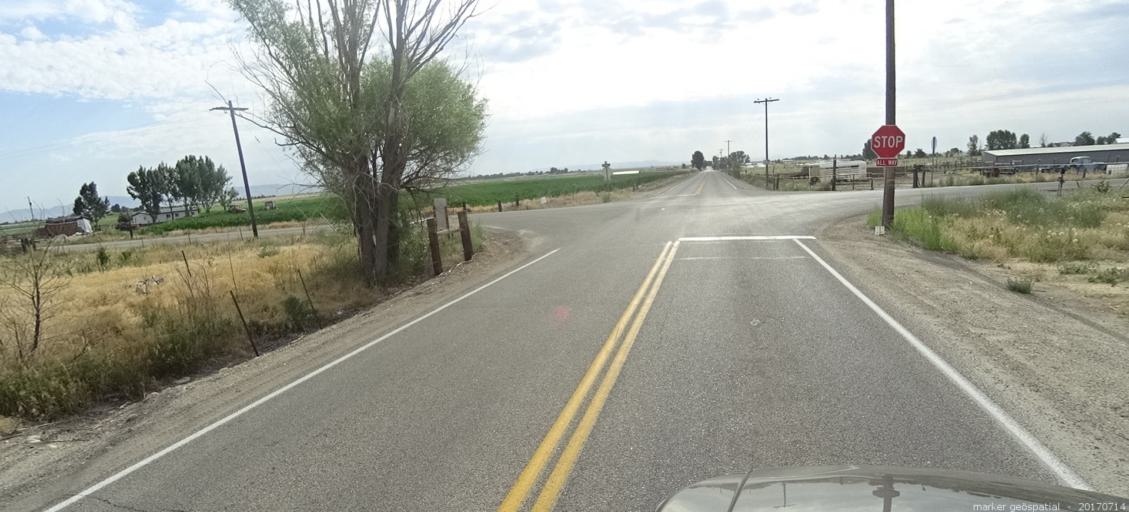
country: US
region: Idaho
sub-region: Ada County
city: Kuna
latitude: 43.4736
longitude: -116.3550
